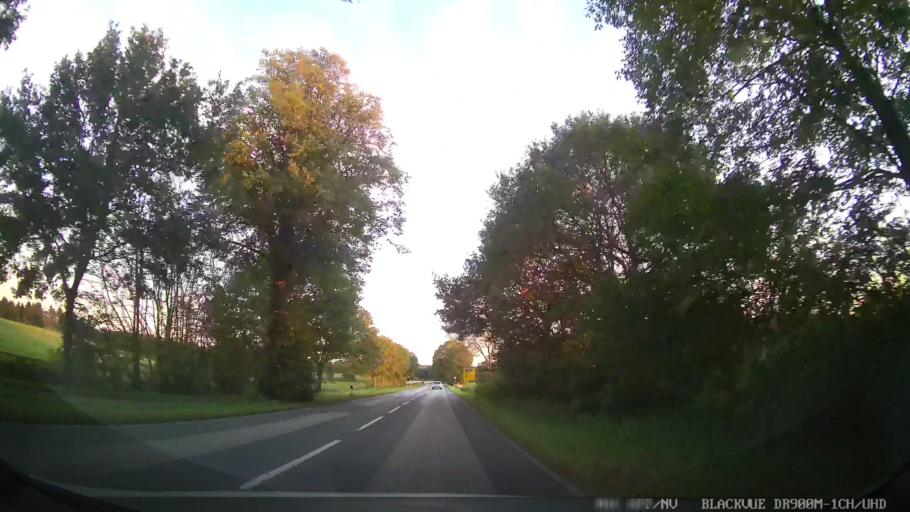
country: DE
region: Schleswig-Holstein
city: Susel
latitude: 54.0163
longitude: 10.6867
